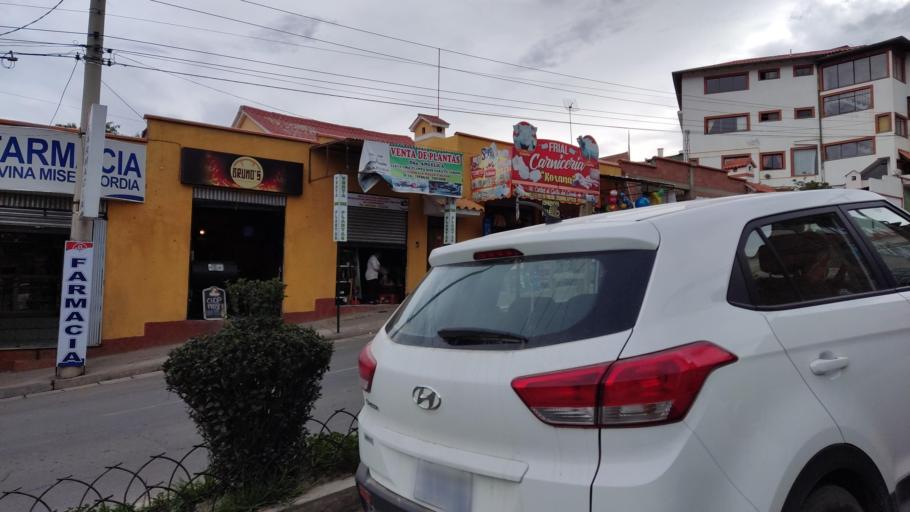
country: BO
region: La Paz
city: La Paz
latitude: -16.5675
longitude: -68.0898
